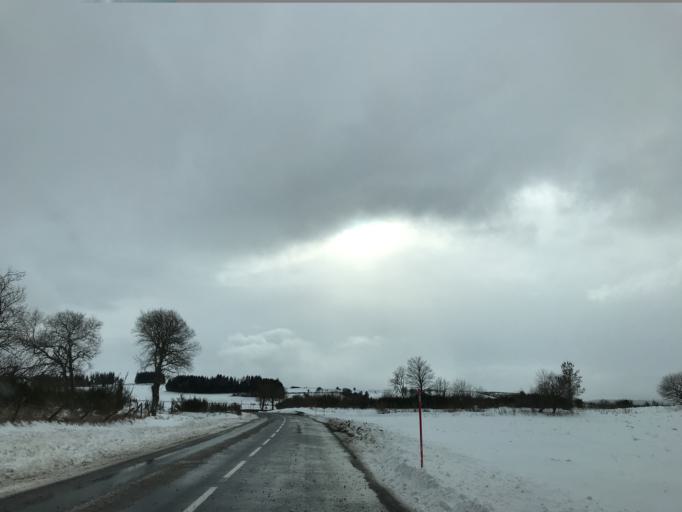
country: FR
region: Auvergne
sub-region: Departement du Puy-de-Dome
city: Aydat
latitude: 45.6802
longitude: 2.9360
